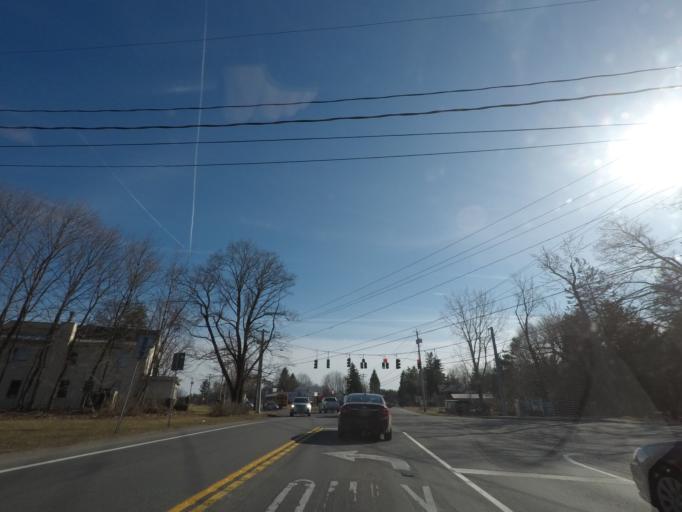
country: US
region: New York
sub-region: Saratoga County
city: Ballston Spa
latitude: 42.9886
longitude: -73.8523
